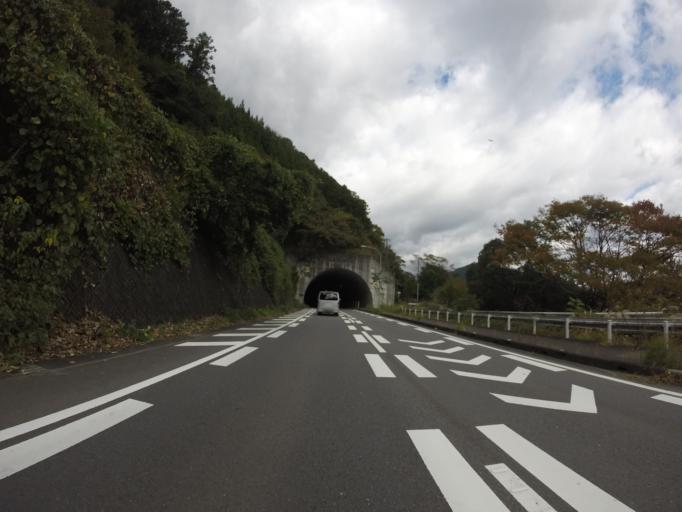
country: JP
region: Shizuoka
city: Kanaya
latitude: 35.0528
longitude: 138.0903
